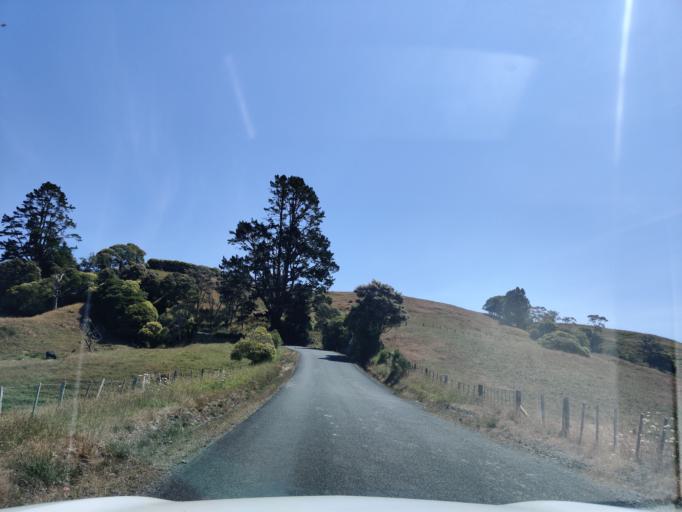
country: NZ
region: Auckland
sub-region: Auckland
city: Red Hill
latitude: -37.0634
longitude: 175.0784
